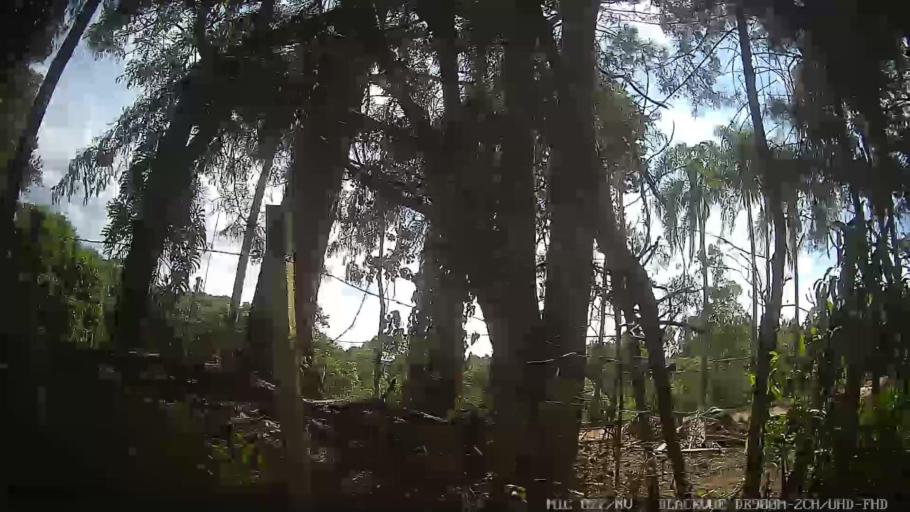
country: BR
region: Sao Paulo
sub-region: Atibaia
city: Atibaia
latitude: -23.0851
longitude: -46.5425
